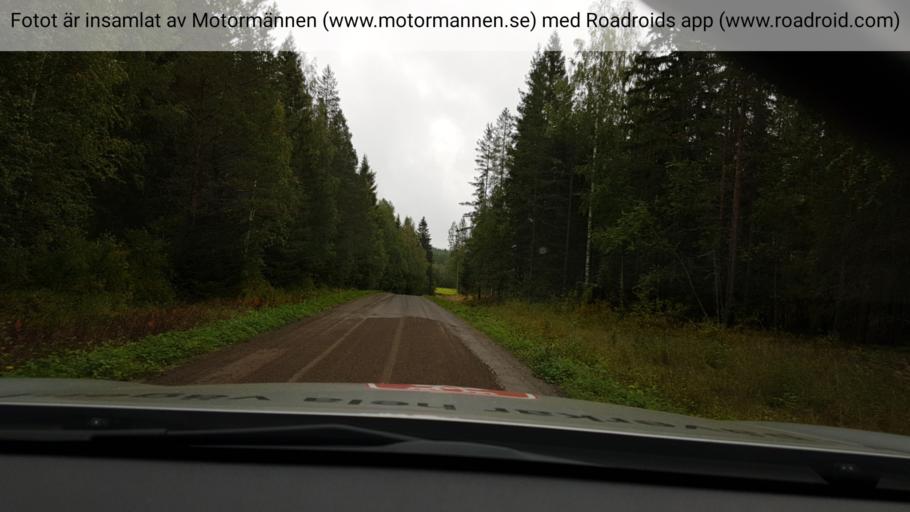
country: SE
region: Vaesterbotten
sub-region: Robertsfors Kommun
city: Robertsfors
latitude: 64.1923
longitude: 20.7181
